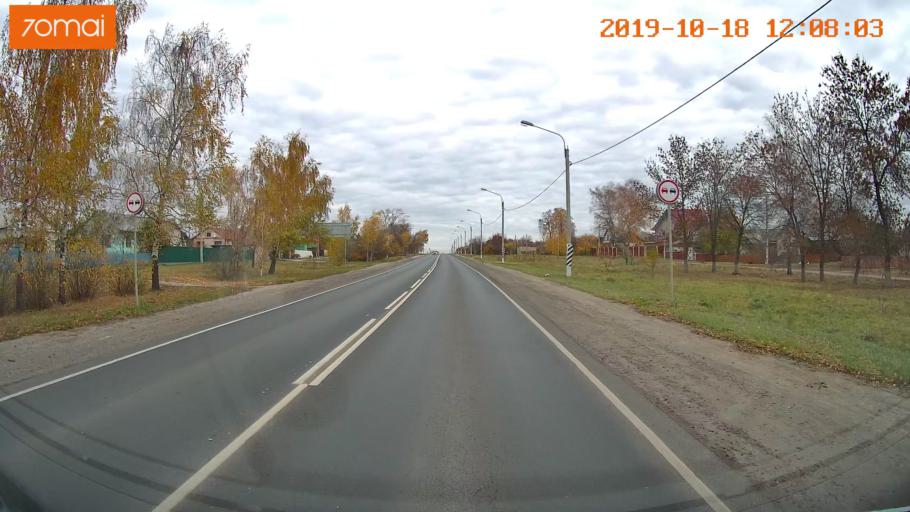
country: RU
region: Rjazan
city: Zakharovo
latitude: 54.3725
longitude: 39.2878
